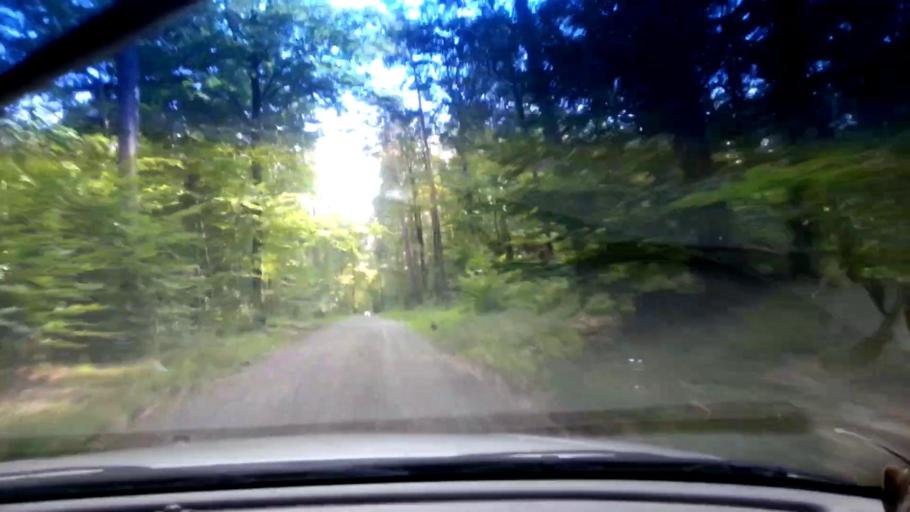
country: DE
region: Bavaria
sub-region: Upper Franconia
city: Lauter
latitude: 49.9621
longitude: 10.7839
